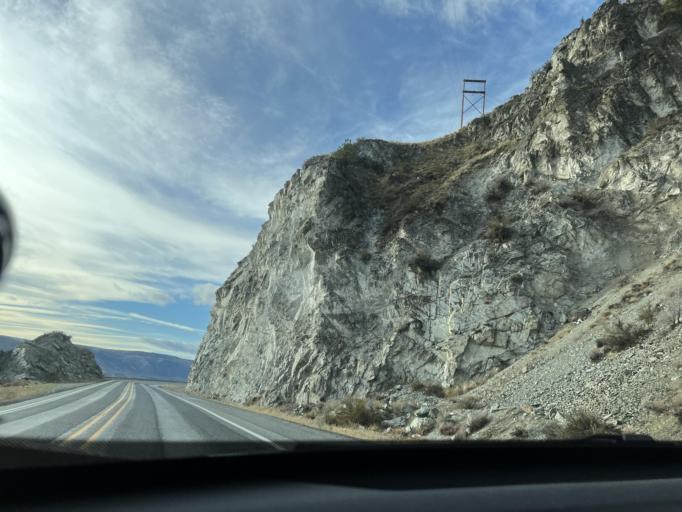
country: US
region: Washington
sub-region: Chelan County
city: Chelan
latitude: 47.8580
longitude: -119.9575
